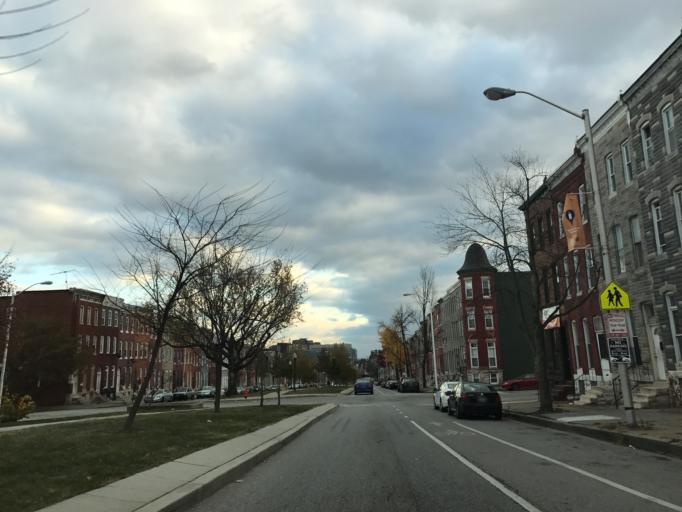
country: US
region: Maryland
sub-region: City of Baltimore
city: Baltimore
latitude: 39.3111
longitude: -76.5952
